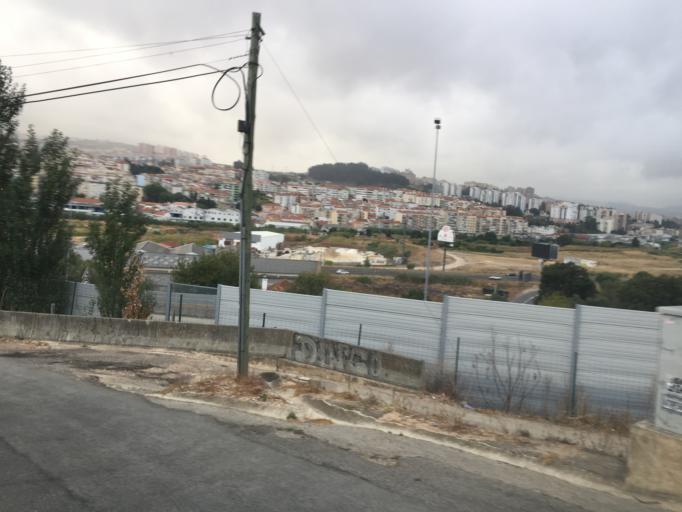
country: PT
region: Lisbon
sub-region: Odivelas
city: Povoa de Santo Adriao
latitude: 38.7964
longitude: -9.1554
